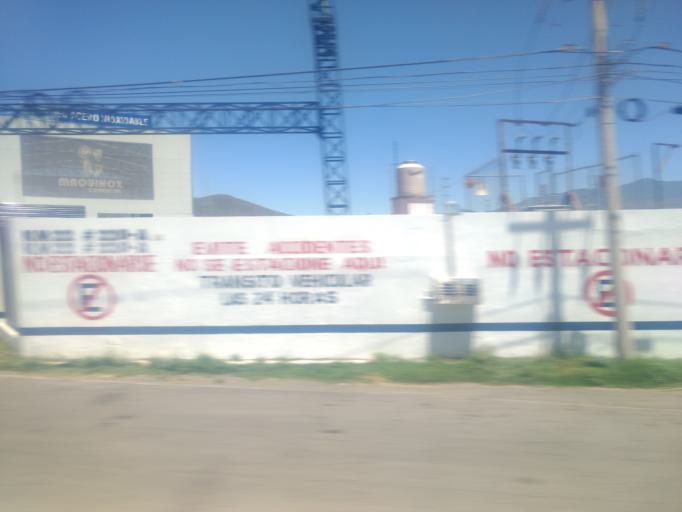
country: MX
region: Jalisco
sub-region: Tlajomulco de Zuniga
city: Santa Cruz de las Flores
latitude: 20.4815
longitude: -103.4971
